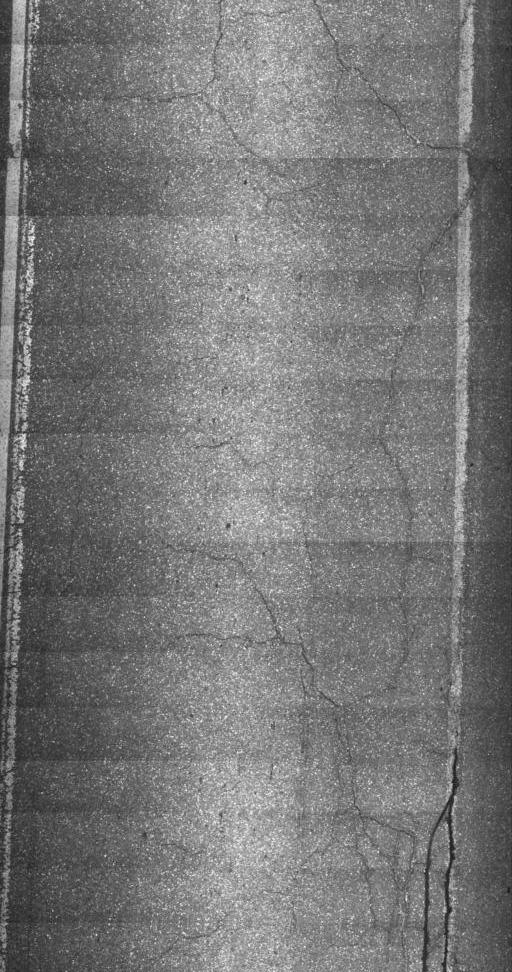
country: US
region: Vermont
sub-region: Lamoille County
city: Hyde Park
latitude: 44.6661
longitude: -72.6046
